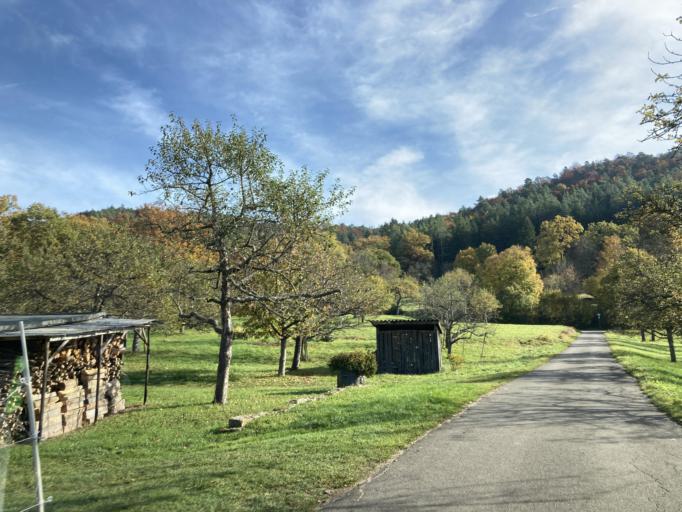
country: DE
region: Baden-Wuerttemberg
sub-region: Tuebingen Region
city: Rottenburg
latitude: 48.4685
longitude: 8.9788
